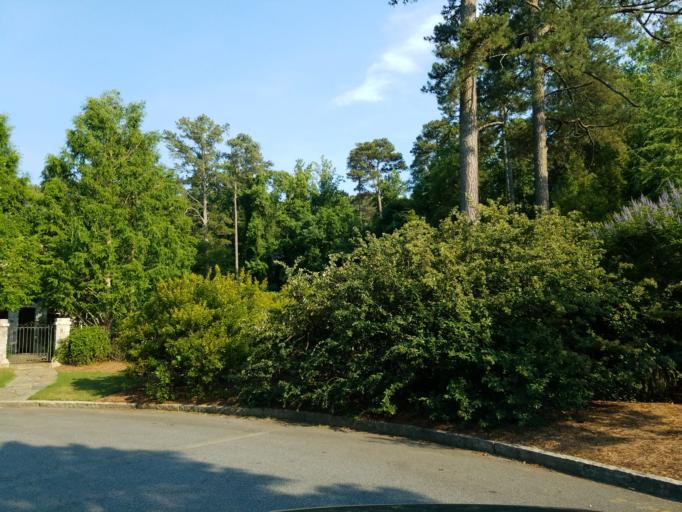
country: US
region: Georgia
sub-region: Cobb County
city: Vinings
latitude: 33.8580
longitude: -84.4402
